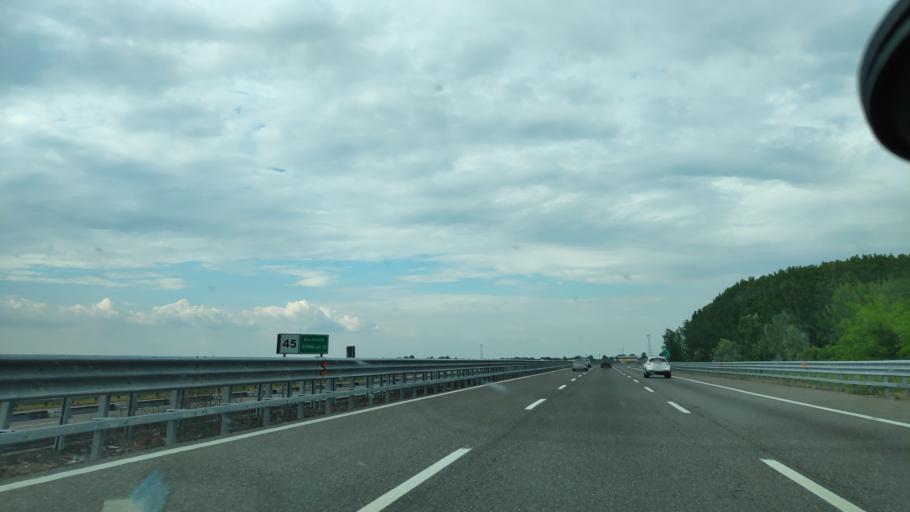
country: IT
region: Lombardy
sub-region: Provincia di Pavia
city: Silvano Pietra
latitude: 45.0543
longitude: 8.9522
